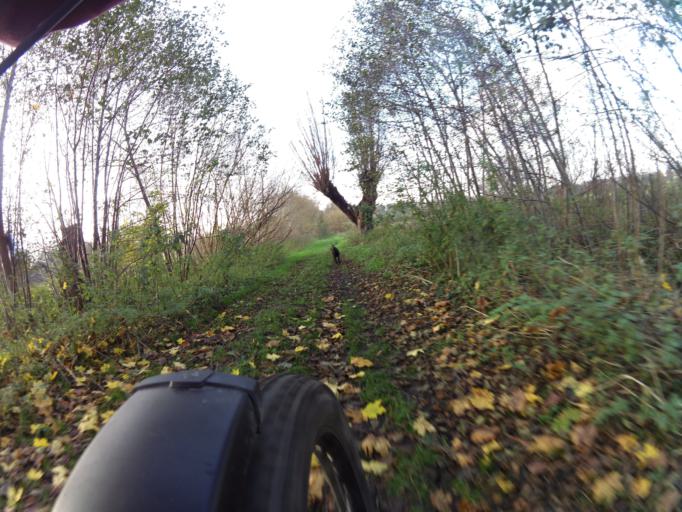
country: PL
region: Pomeranian Voivodeship
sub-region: Powiat pucki
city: Krokowa
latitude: 54.7748
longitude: 18.1703
